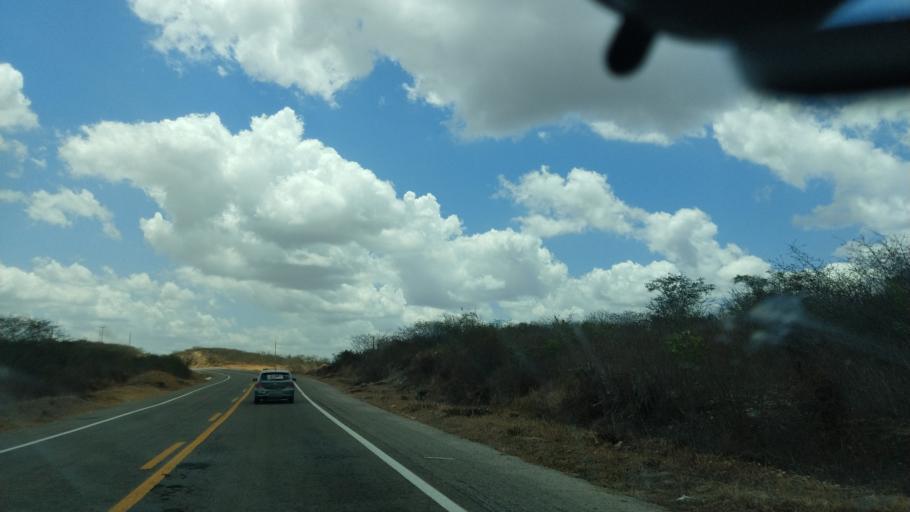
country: BR
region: Rio Grande do Norte
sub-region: Cerro Cora
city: Cerro Cora
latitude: -6.1881
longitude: -36.2354
